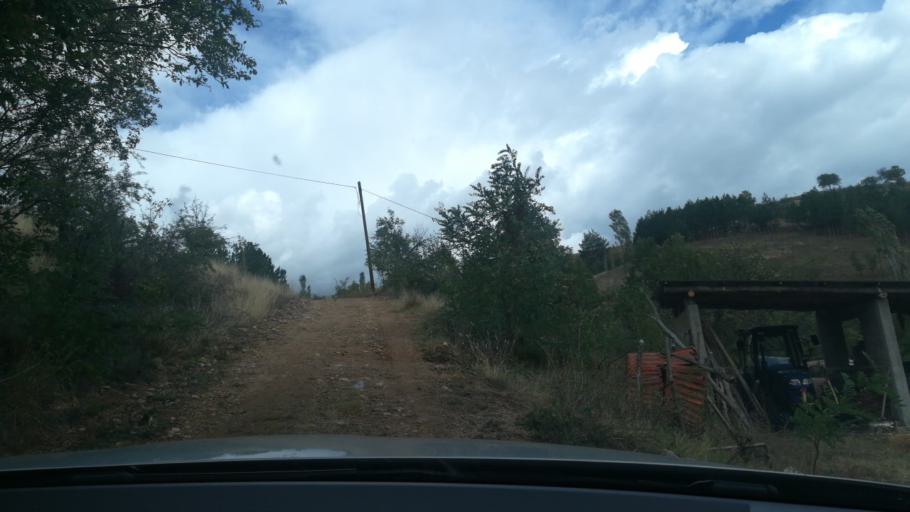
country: MK
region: Makedonska Kamenica
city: Makedonska Kamenica
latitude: 42.0030
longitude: 22.6068
